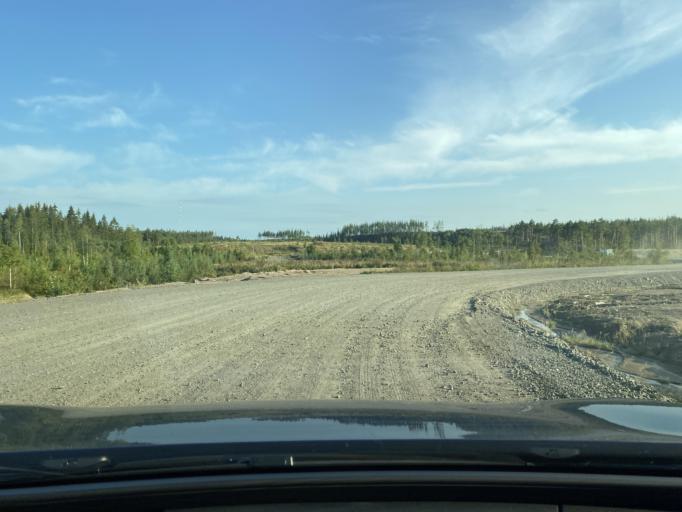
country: FI
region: Kymenlaakso
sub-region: Kouvola
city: Iitti
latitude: 60.8806
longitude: 26.4915
